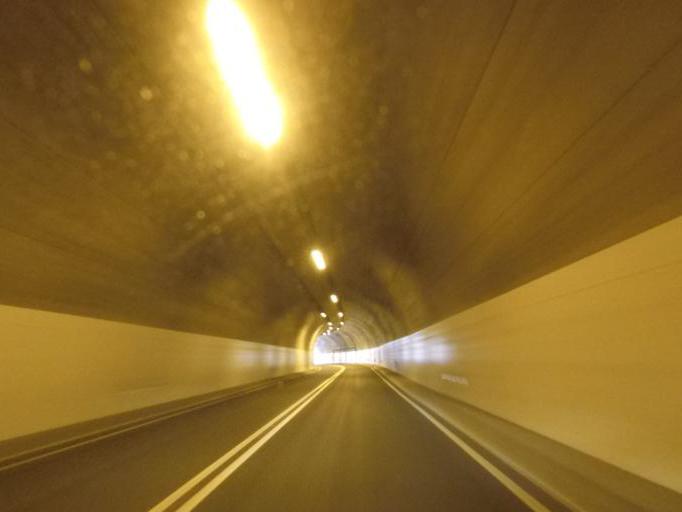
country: PT
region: Madeira
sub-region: Machico
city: Machico
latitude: 32.7341
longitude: -16.7950
